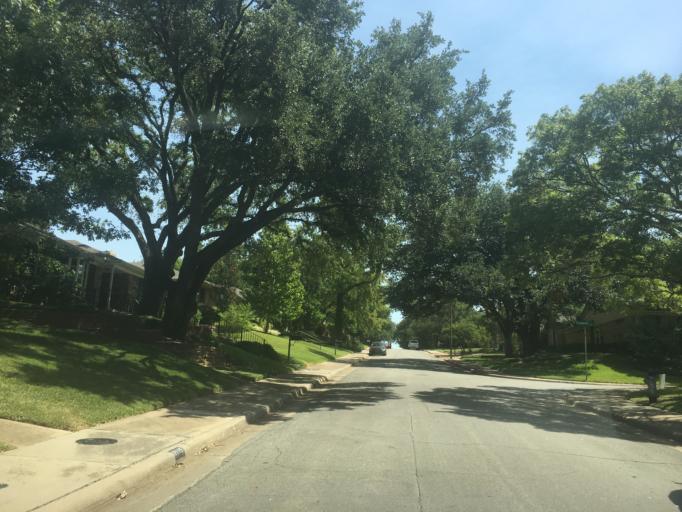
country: US
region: Texas
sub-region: Dallas County
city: University Park
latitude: 32.8757
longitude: -96.7404
